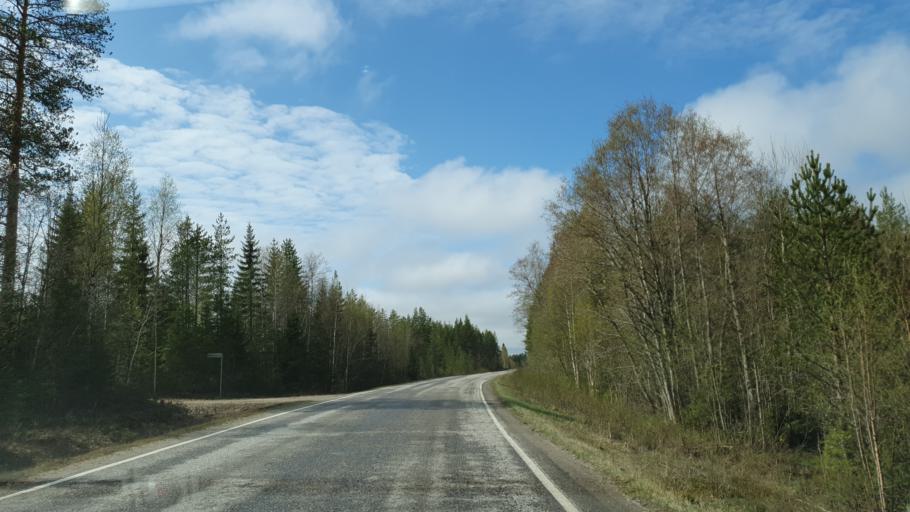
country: FI
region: Kainuu
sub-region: Kehys-Kainuu
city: Kuhmo
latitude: 64.1250
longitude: 29.6155
